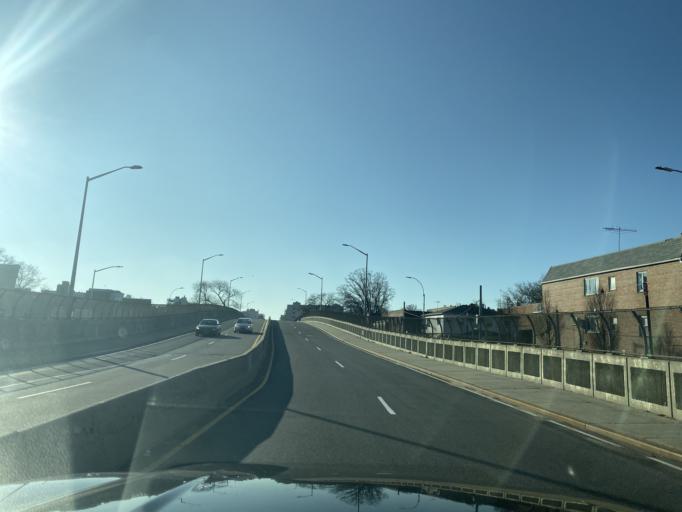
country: US
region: New York
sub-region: Kings County
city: Coney Island
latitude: 40.5864
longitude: -73.9604
